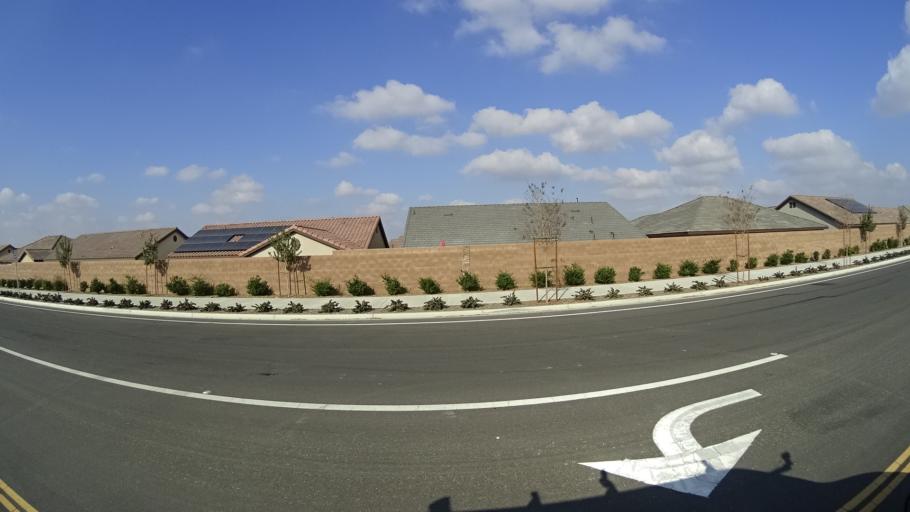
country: US
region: California
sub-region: Kern County
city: Greenacres
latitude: 35.2885
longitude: -119.1045
